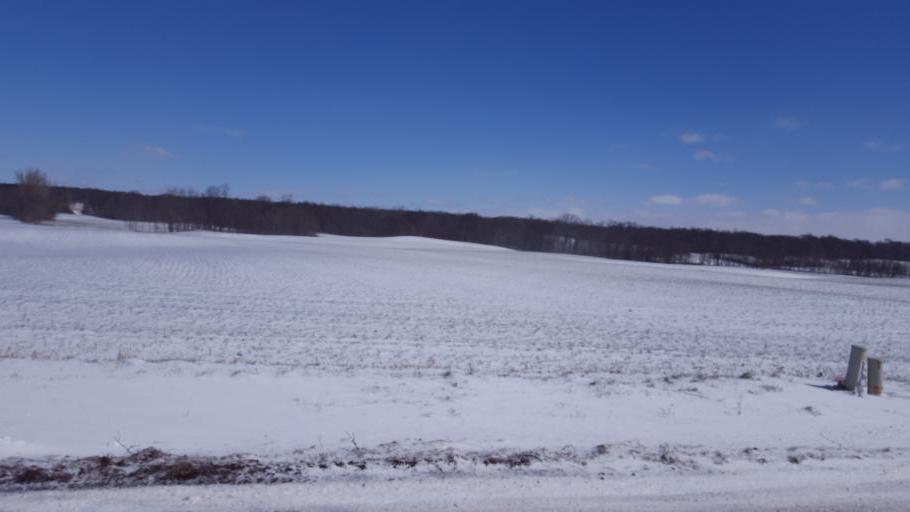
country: US
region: Ohio
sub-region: Knox County
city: Fredericktown
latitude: 40.4773
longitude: -82.6757
